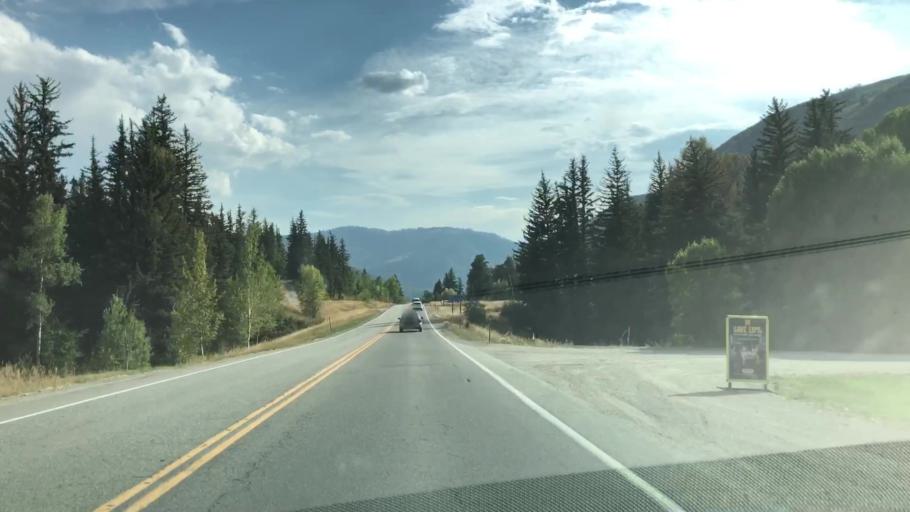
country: US
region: Wyoming
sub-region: Teton County
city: Hoback
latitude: 43.3407
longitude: -110.7230
